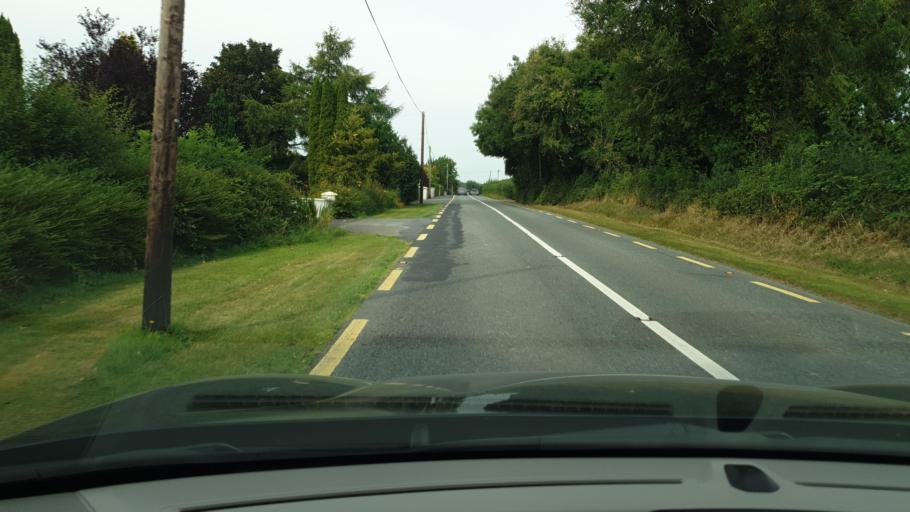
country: IE
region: Leinster
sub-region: An Mhi
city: Trim
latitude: 53.6322
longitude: -6.8027
